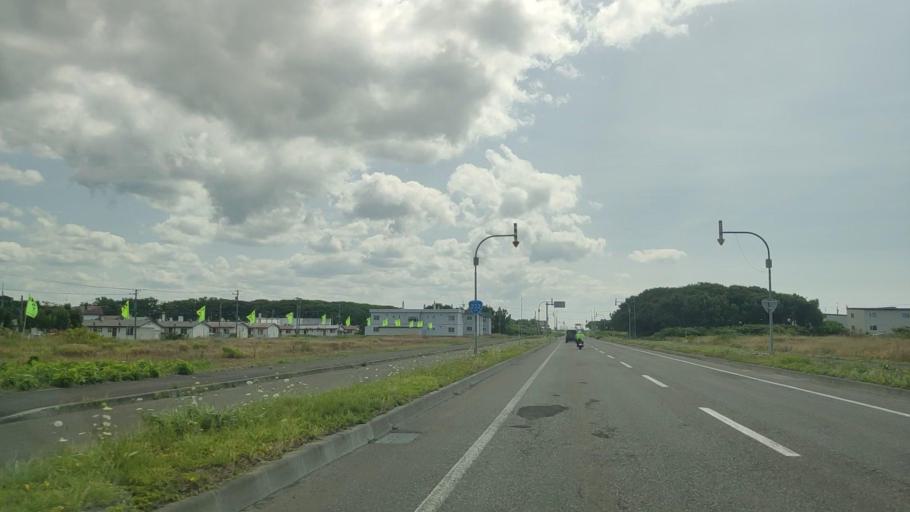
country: JP
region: Hokkaido
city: Makubetsu
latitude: 44.8798
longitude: 141.7499
